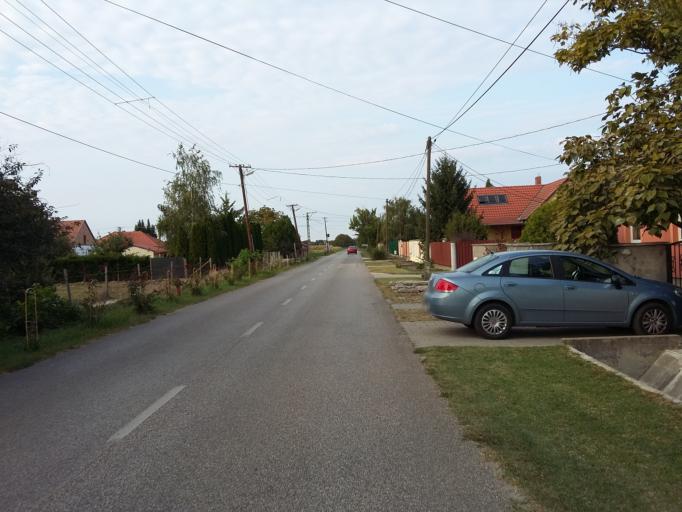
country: HU
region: Csongrad
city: Szeged
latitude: 46.2098
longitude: 20.1077
